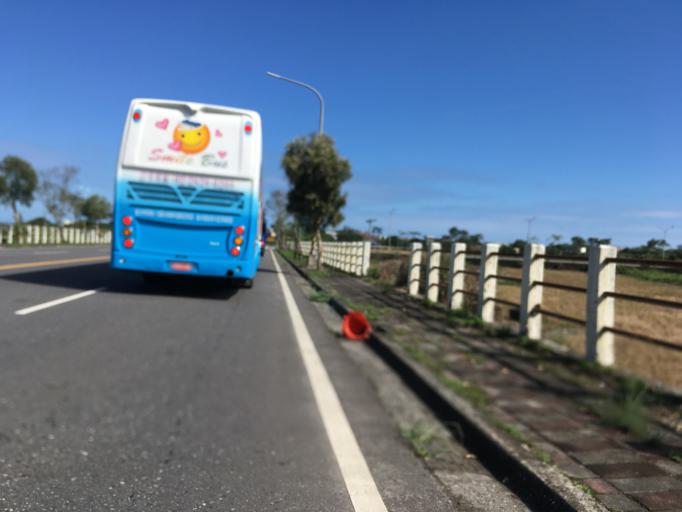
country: TW
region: Taiwan
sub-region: Yilan
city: Yilan
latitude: 24.6165
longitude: 121.8454
